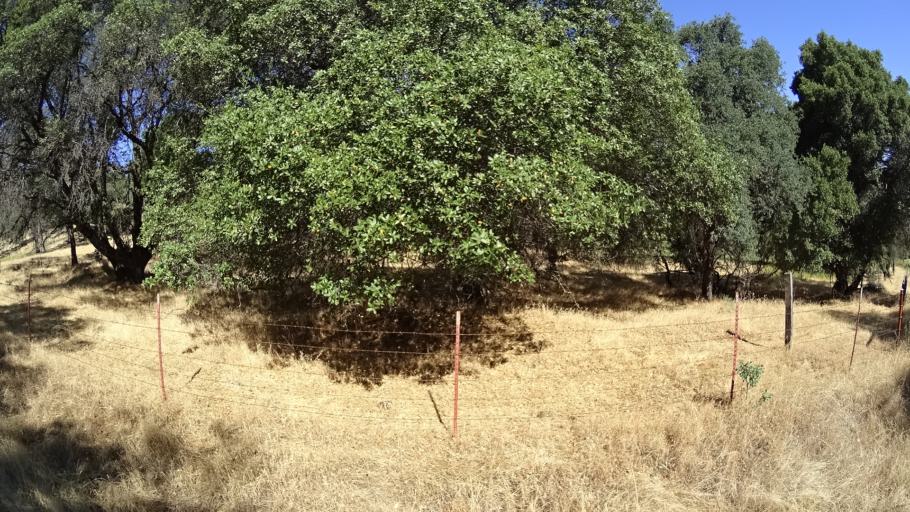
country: US
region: California
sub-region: Calaveras County
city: Murphys
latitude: 38.0834
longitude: -120.4759
